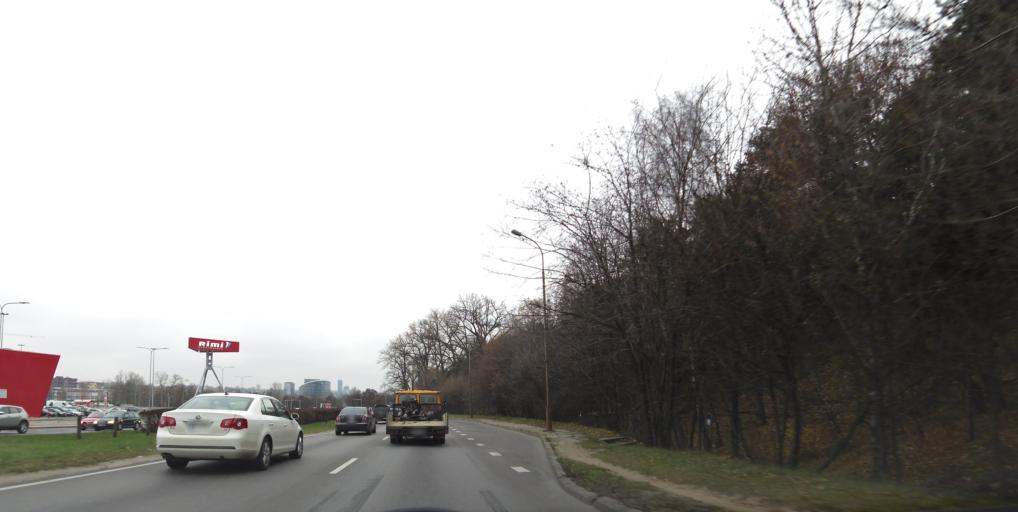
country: LT
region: Vilnius County
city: Seskine
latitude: 54.7065
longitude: 25.2668
